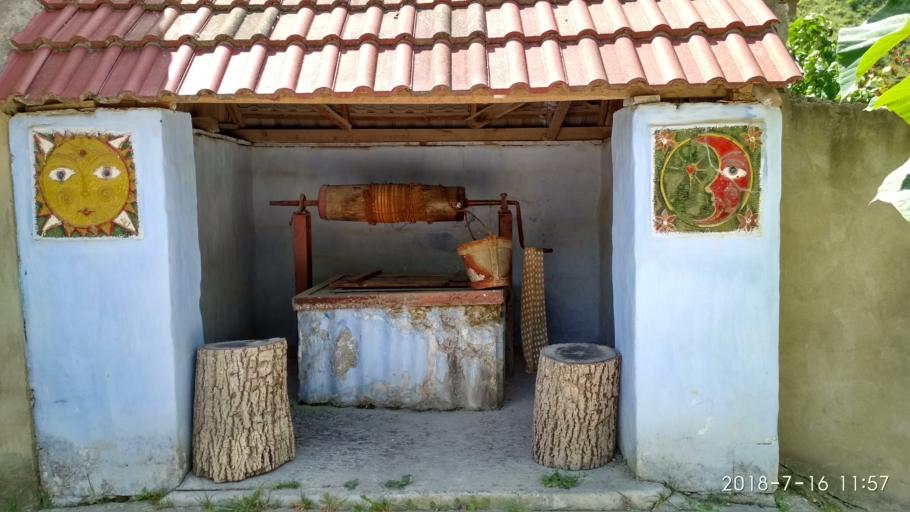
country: MD
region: Telenesti
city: Cocieri
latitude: 47.3021
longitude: 28.9663
